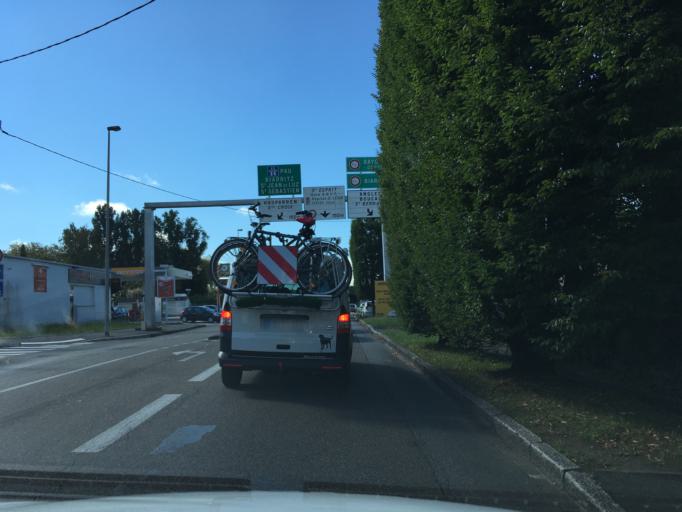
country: FR
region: Aquitaine
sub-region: Departement des Pyrenees-Atlantiques
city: Boucau
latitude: 43.5054
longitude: -1.4673
